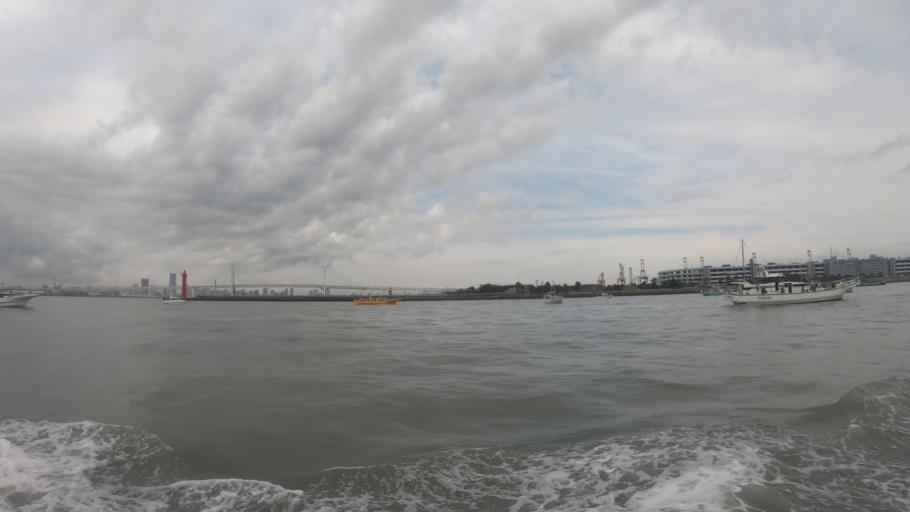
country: JP
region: Kanagawa
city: Yokohama
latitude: 35.4474
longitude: 139.6987
